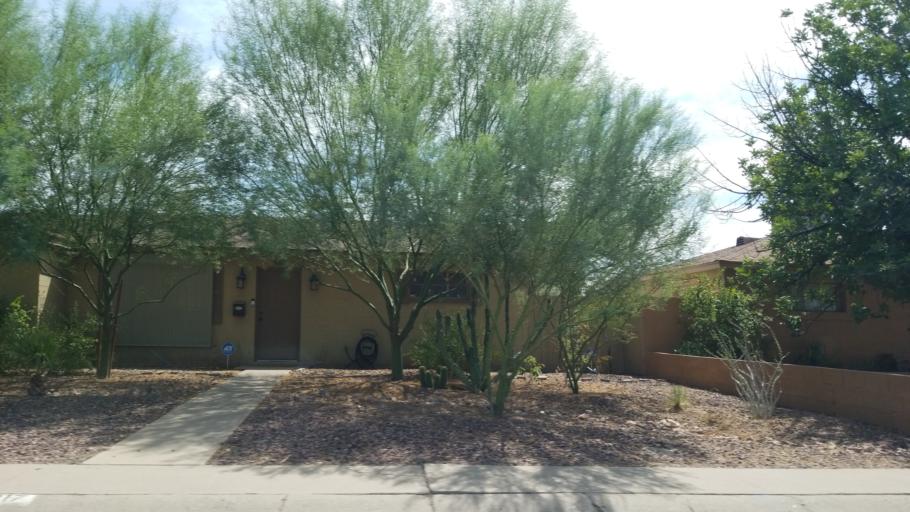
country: US
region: Arizona
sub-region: Maricopa County
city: Glendale
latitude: 33.5593
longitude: -112.1256
